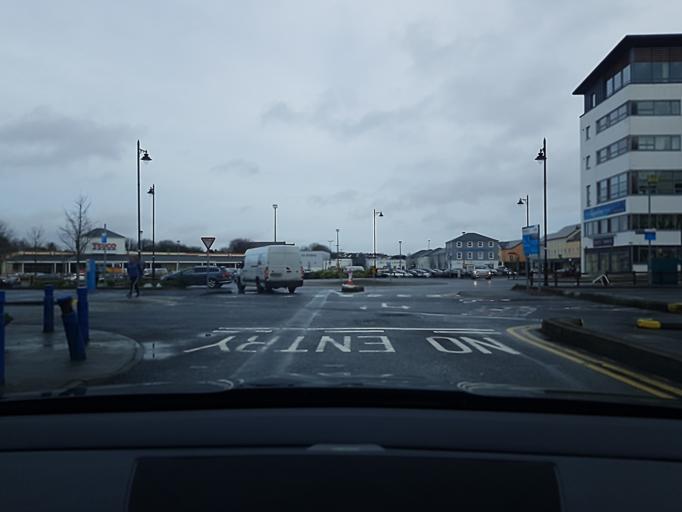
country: IE
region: Connaught
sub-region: Maigh Eo
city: Castlebar
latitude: 53.8540
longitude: -9.3042
